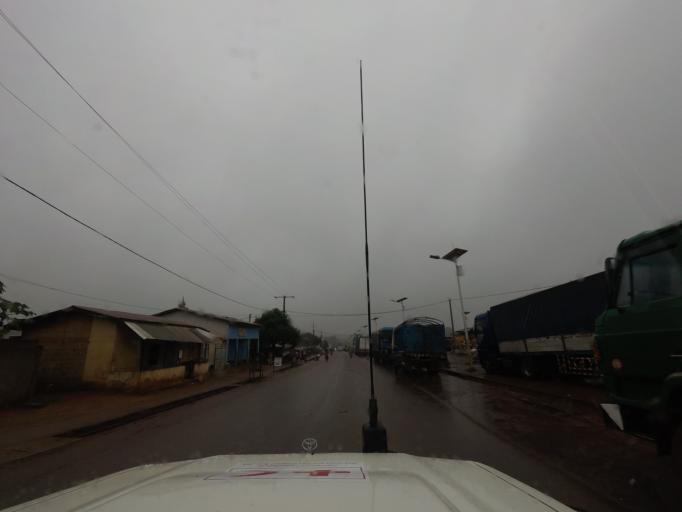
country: GN
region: Nzerekore
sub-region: Nzerekore Prefecture
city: Nzerekore
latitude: 7.7405
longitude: -8.8251
